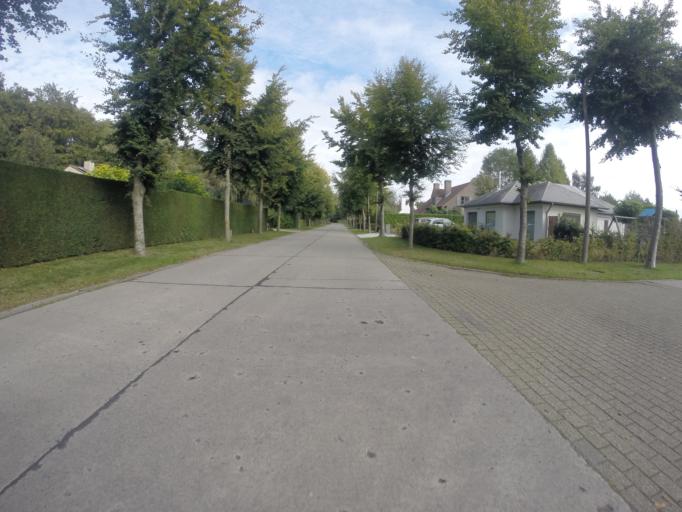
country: BE
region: Flanders
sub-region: Provincie Oost-Vlaanderen
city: Aalter
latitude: 51.0704
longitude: 3.4591
